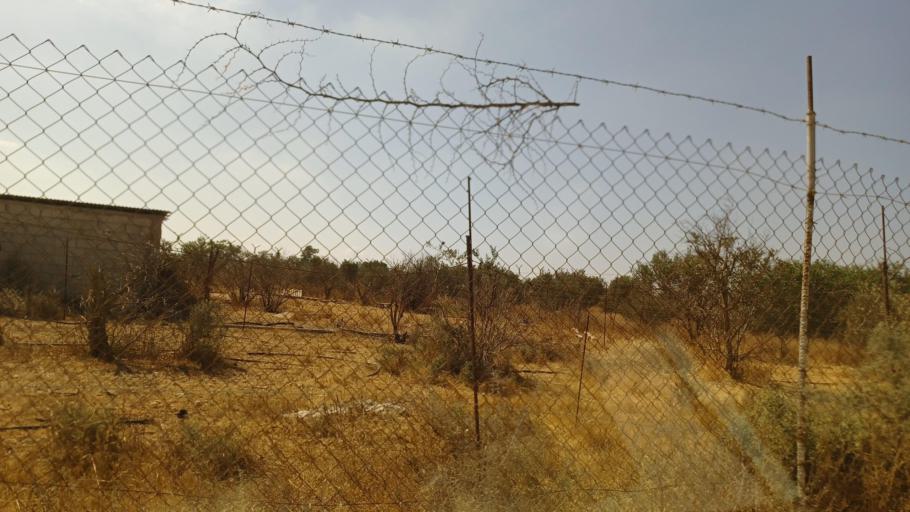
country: CY
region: Ammochostos
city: Acheritou
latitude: 35.0707
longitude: 33.8660
